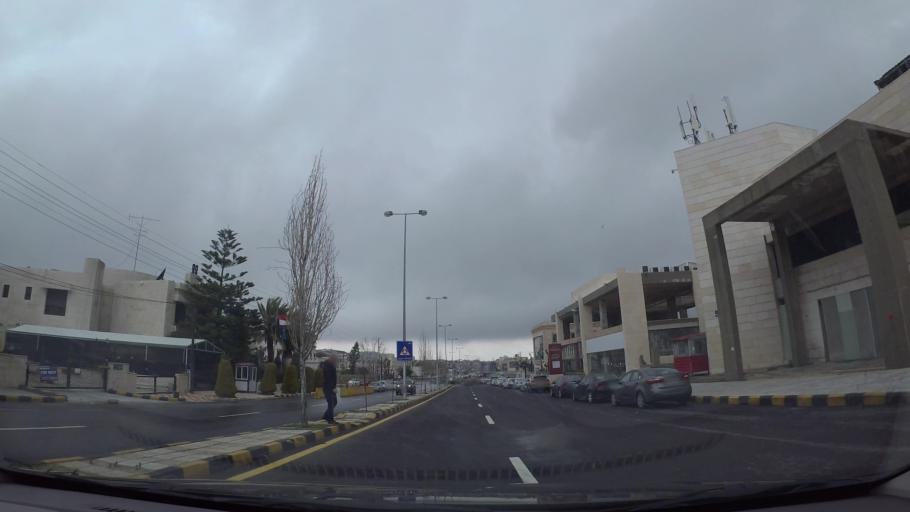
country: JO
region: Amman
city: Al Bunayyat ash Shamaliyah
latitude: 31.9414
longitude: 35.8800
